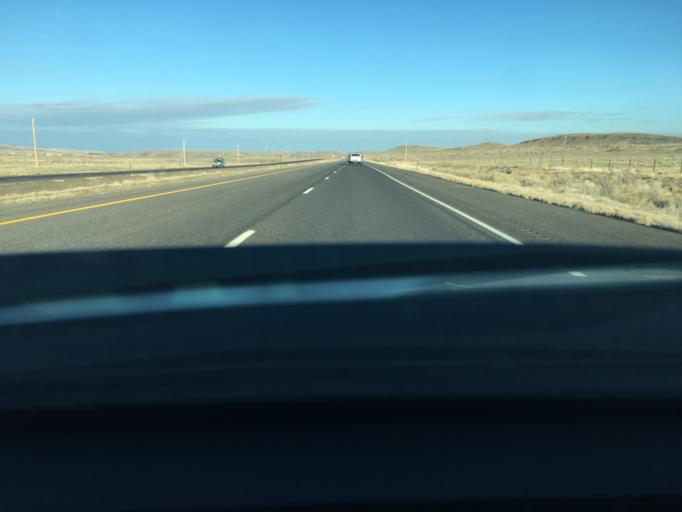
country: US
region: Colorado
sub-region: Mesa County
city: Clifton
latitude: 38.9017
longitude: -108.3677
